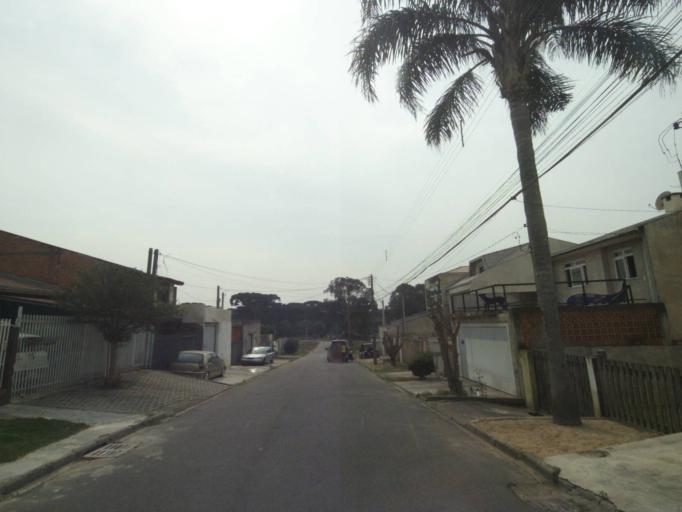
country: BR
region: Parana
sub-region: Sao Jose Dos Pinhais
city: Sao Jose dos Pinhais
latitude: -25.5279
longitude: -49.2768
